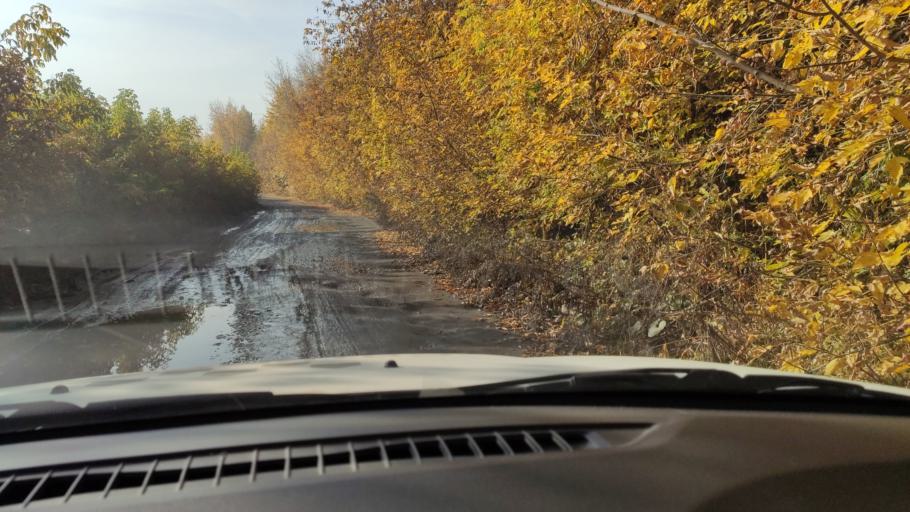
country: RU
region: Perm
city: Kondratovo
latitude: 58.0090
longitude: 56.1577
